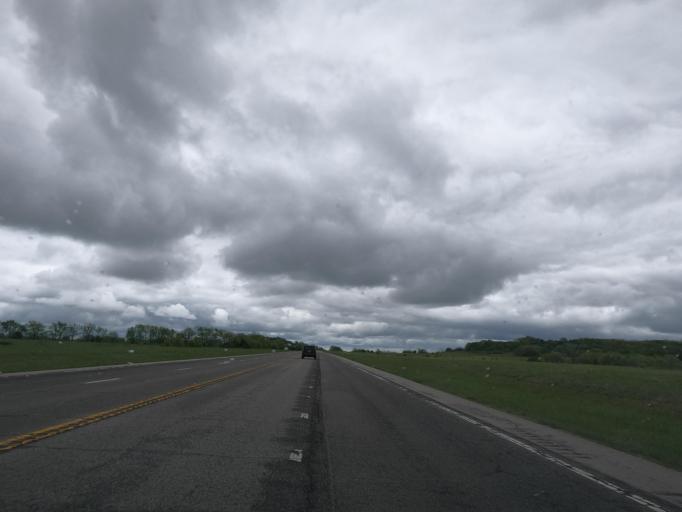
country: US
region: Kansas
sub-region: Montgomery County
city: Cherryvale
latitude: 37.3466
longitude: -95.4819
